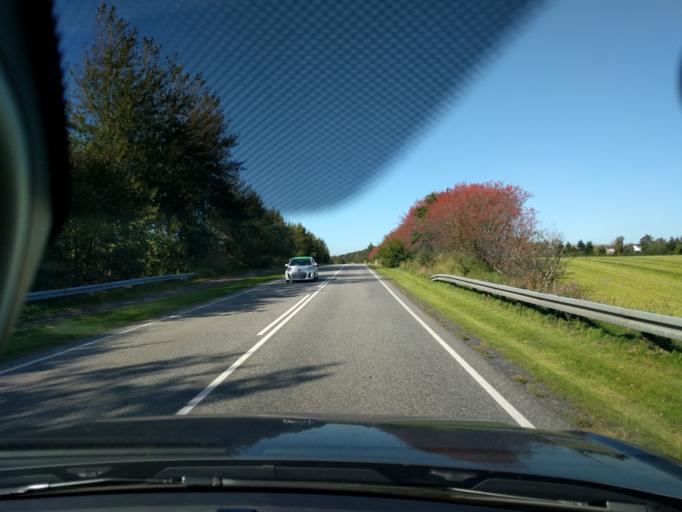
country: DK
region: North Denmark
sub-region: Mariagerfjord Kommune
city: Hobro
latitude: 56.6966
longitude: 9.6480
